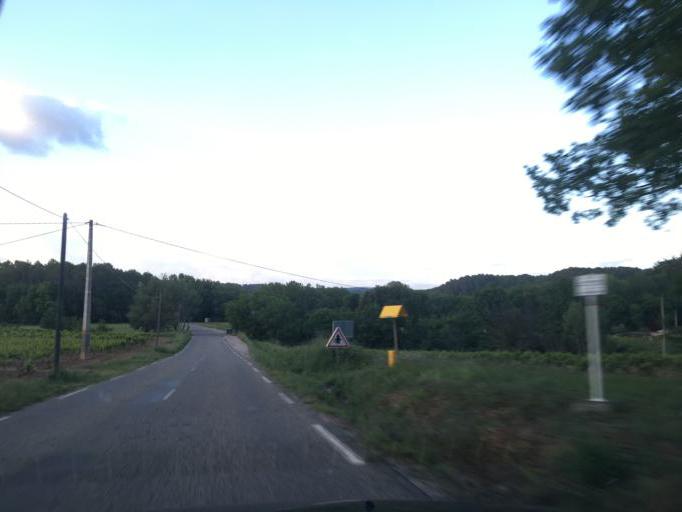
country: FR
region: Provence-Alpes-Cote d'Azur
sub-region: Departement du Var
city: Carces
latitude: 43.4954
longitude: 6.2210
